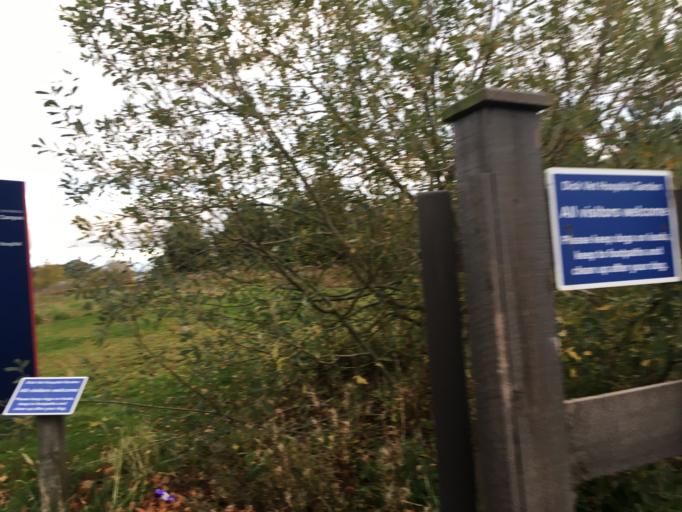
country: GB
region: Scotland
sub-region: Midlothian
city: Penicuik
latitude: 55.8646
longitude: -3.2038
